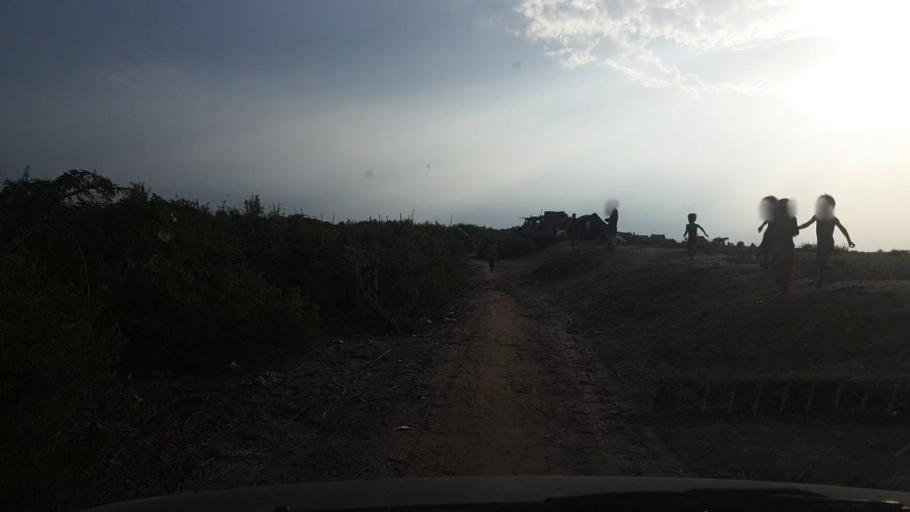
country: PK
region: Sindh
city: Badin
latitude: 24.4285
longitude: 68.6673
